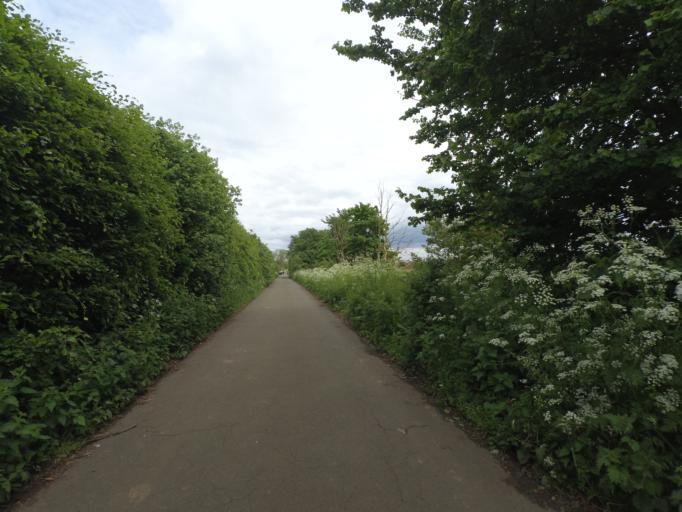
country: GB
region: Scotland
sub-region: East Lothian
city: Ormiston
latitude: 55.9129
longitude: -2.9343
